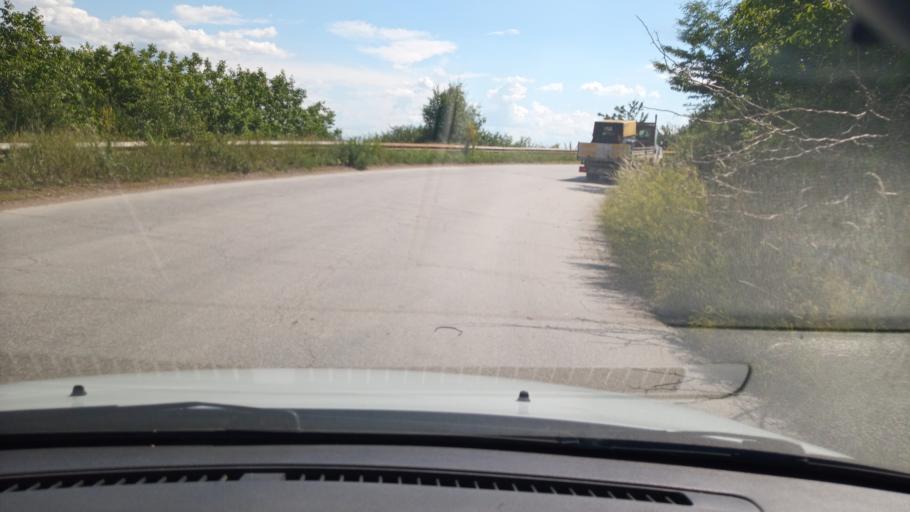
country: BG
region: Pleven
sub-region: Obshtina Dolna Mitropoliya
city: Dolna Mitropoliya
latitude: 43.4389
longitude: 24.5270
